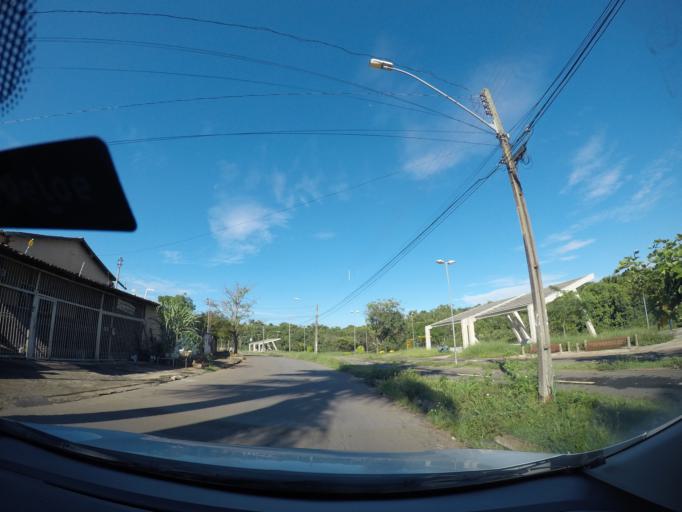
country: BR
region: Goias
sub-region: Goiania
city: Goiania
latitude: -16.7385
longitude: -49.3174
